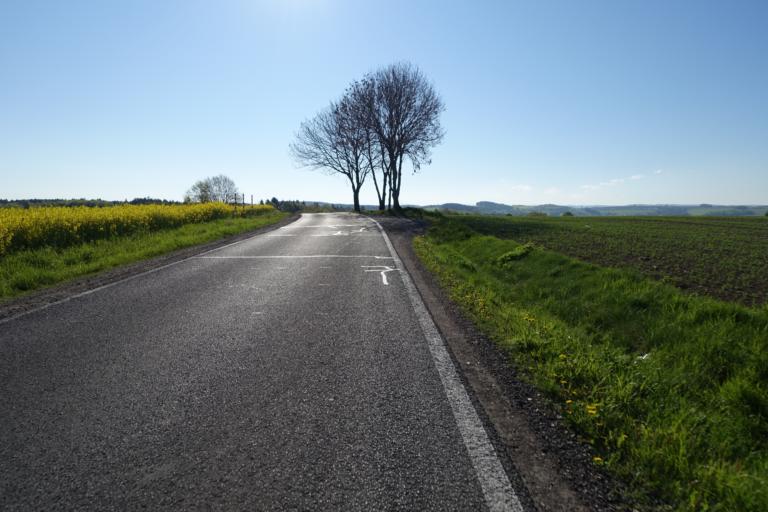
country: DE
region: Saxony
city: Freiberg
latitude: 50.8929
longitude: 13.3681
